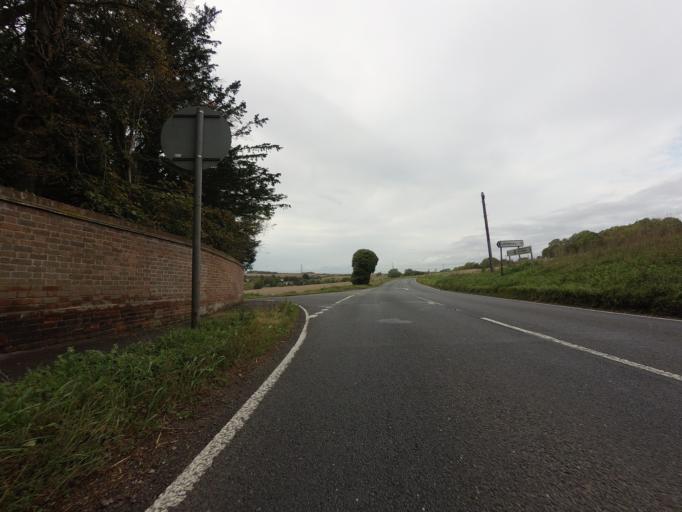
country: GB
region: England
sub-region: Essex
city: Saffron Walden
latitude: 52.0338
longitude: 0.2209
